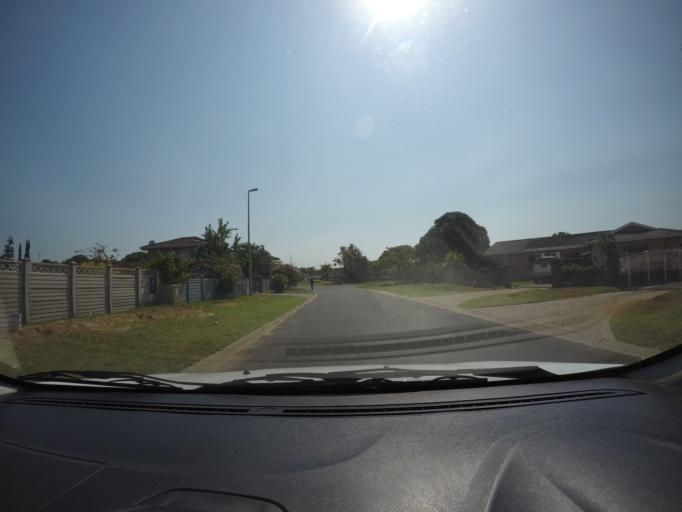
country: ZA
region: KwaZulu-Natal
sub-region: uThungulu District Municipality
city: Richards Bay
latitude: -28.7261
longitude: 32.0404
